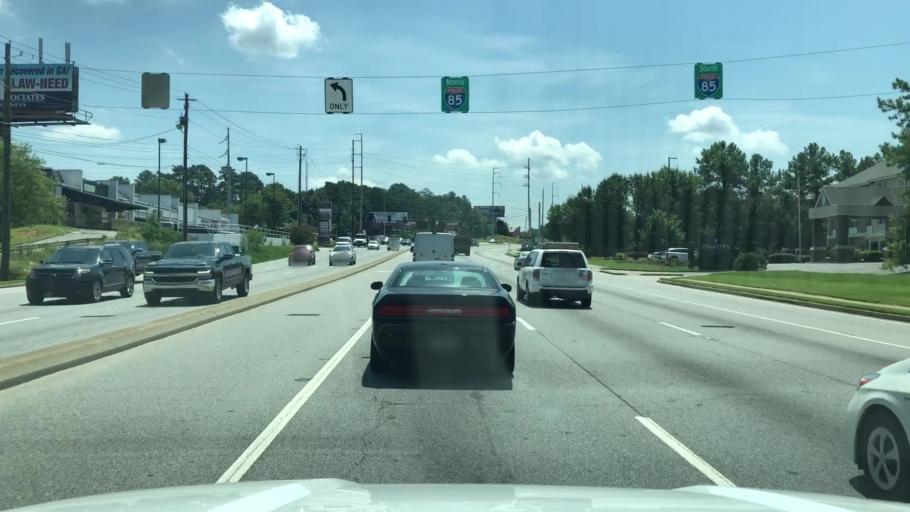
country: US
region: Georgia
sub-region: Gwinnett County
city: Norcross
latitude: 33.9228
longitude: -84.2135
